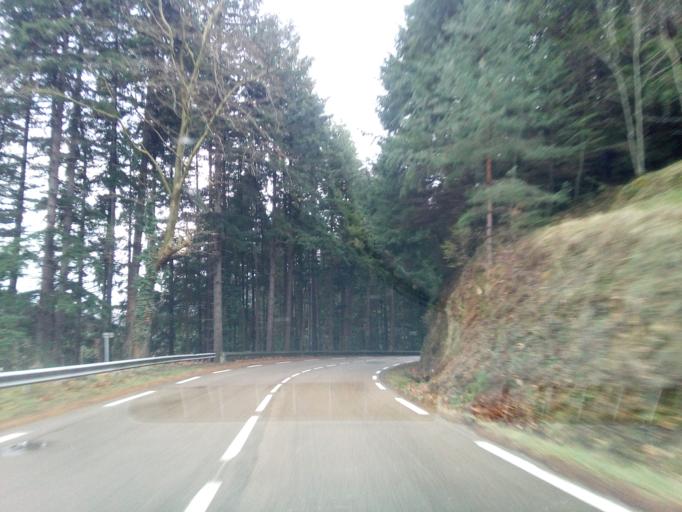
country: FR
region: Rhone-Alpes
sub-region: Departement de l'Ardeche
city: Le Cheylard
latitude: 44.9022
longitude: 4.4840
